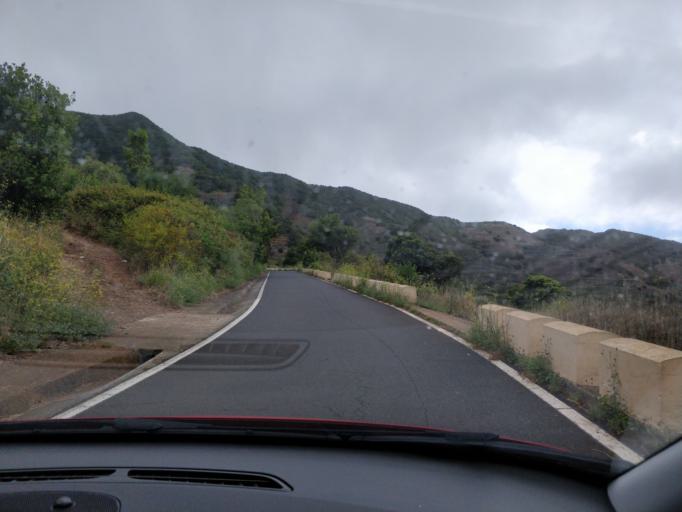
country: ES
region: Canary Islands
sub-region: Provincia de Santa Cruz de Tenerife
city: Santiago del Teide
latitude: 28.3236
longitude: -16.8436
